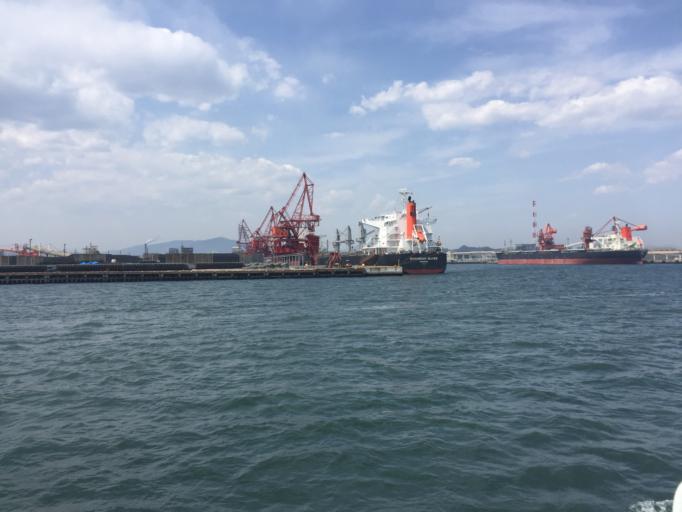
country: JP
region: Fukushima
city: Iwaki
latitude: 36.9274
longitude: 140.8834
